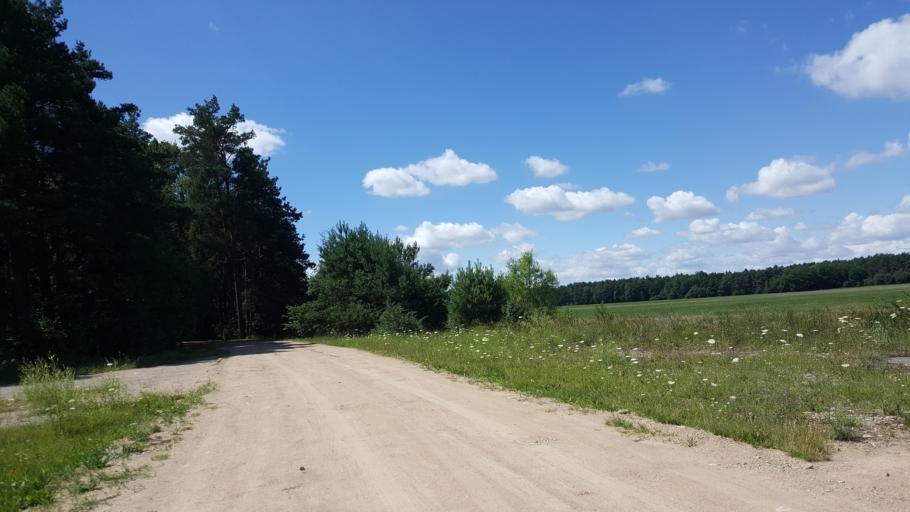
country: BY
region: Brest
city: Kamyanyets
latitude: 52.3301
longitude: 23.9026
